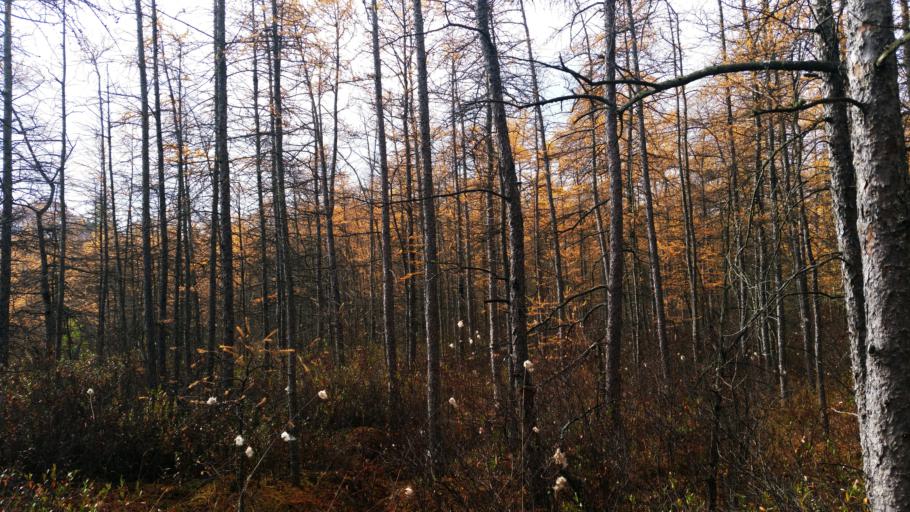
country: US
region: Wisconsin
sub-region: Walworth County
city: East Troy
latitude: 42.8197
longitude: -88.4072
